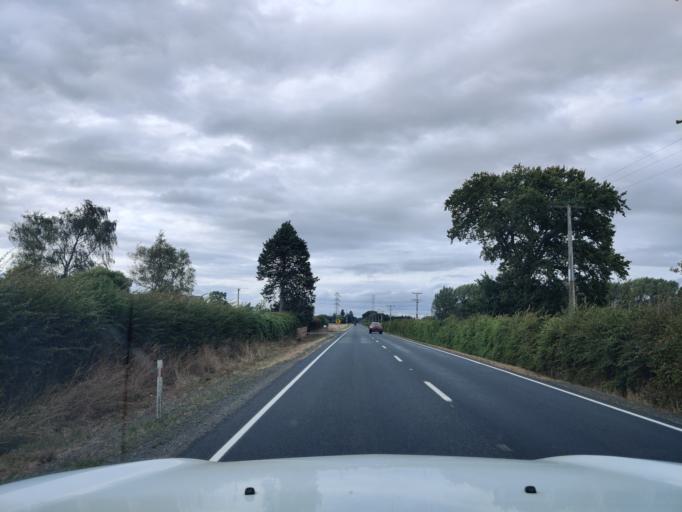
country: NZ
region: Waikato
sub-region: Waipa District
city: Cambridge
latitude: -37.8483
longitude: 175.4536
